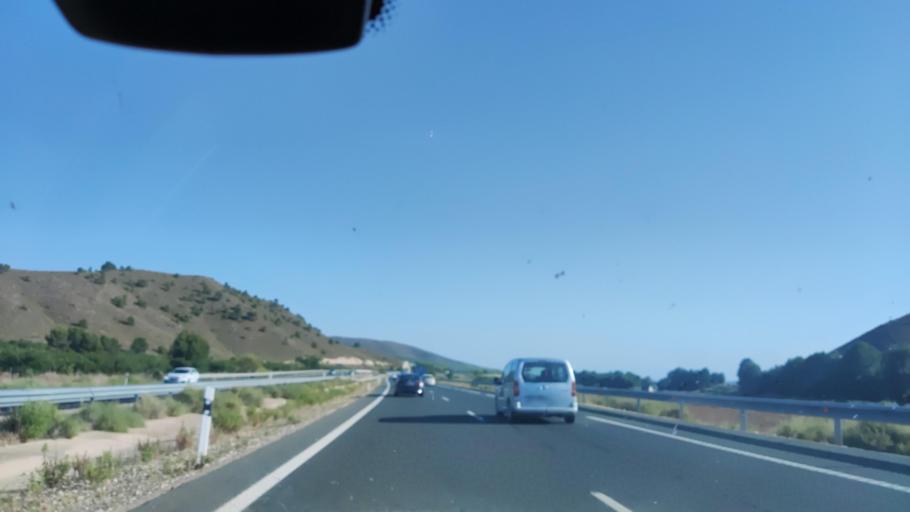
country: ES
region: Castille-La Mancha
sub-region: Provincia de Albacete
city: Tobarra
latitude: 38.6451
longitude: -1.6649
